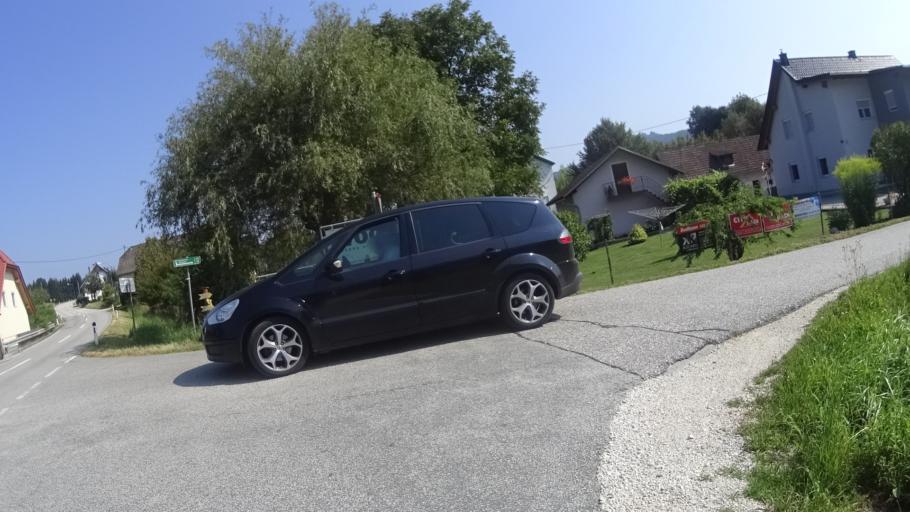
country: AT
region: Carinthia
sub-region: Politischer Bezirk Volkermarkt
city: Gallizien
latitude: 46.5711
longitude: 14.5075
